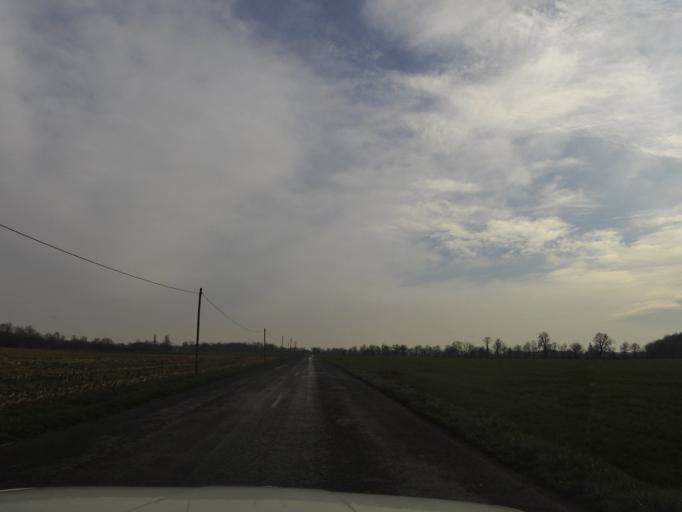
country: FR
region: Rhone-Alpes
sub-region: Departement de l'Ain
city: Villars-les-Dombes
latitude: 46.0458
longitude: 5.0724
